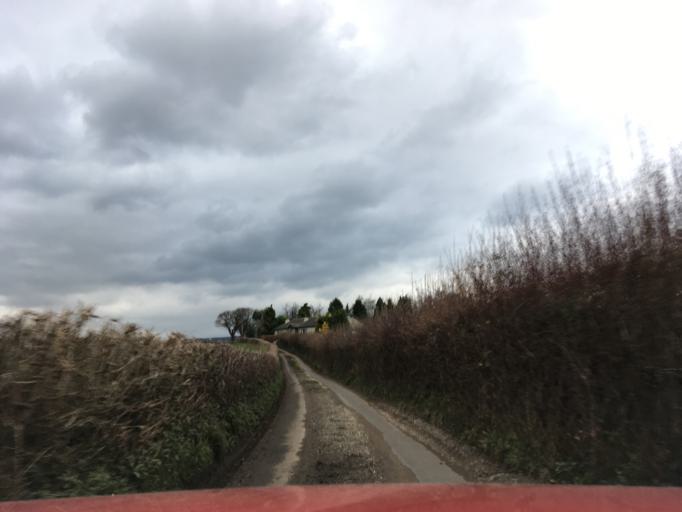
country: GB
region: Wales
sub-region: Newport
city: Llanvaches
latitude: 51.6114
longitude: -2.8071
